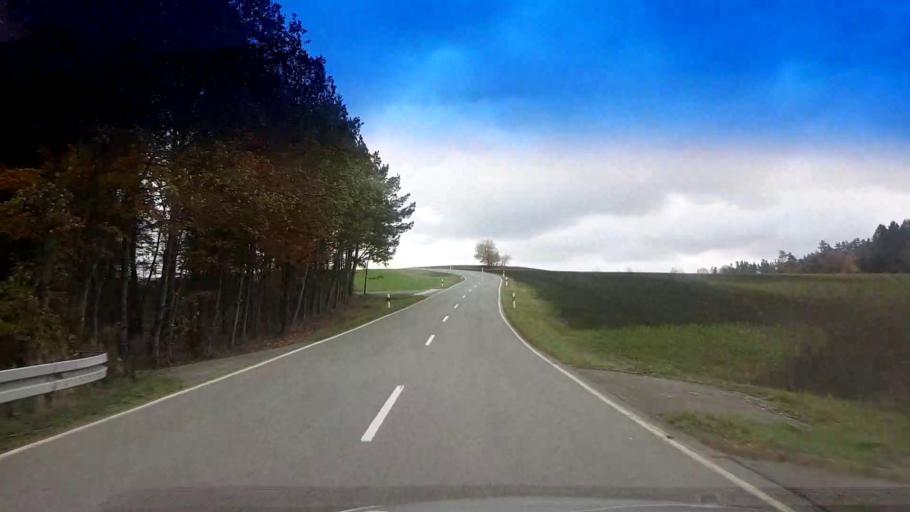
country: DE
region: Bavaria
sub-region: Upper Franconia
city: Poxdorf
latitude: 49.9426
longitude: 11.1077
